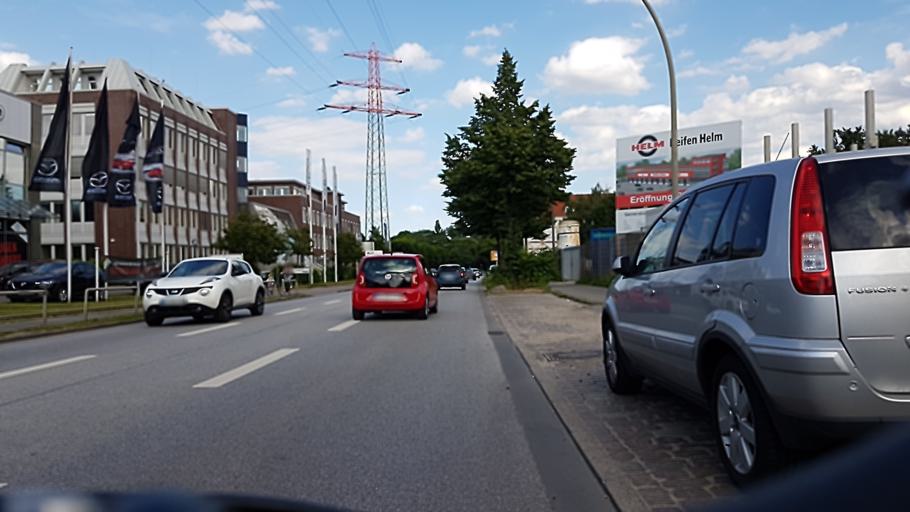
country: DE
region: Hamburg
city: Hamburg-Nord
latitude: 53.6014
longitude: 9.9796
